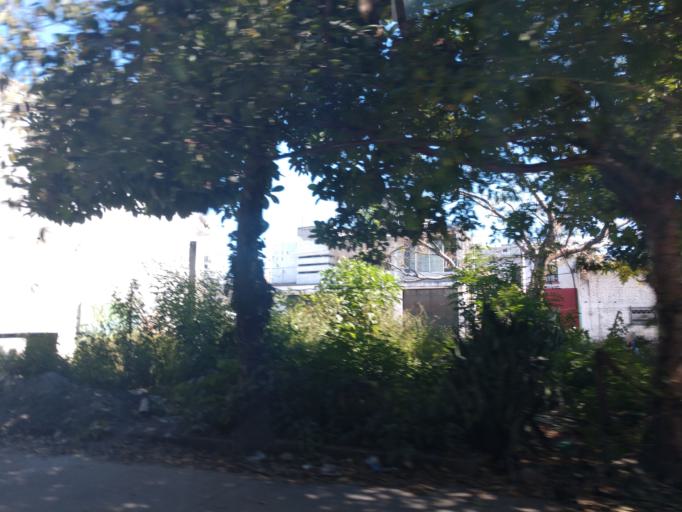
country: MX
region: Nayarit
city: Xalisco
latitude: 21.4713
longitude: -104.8704
